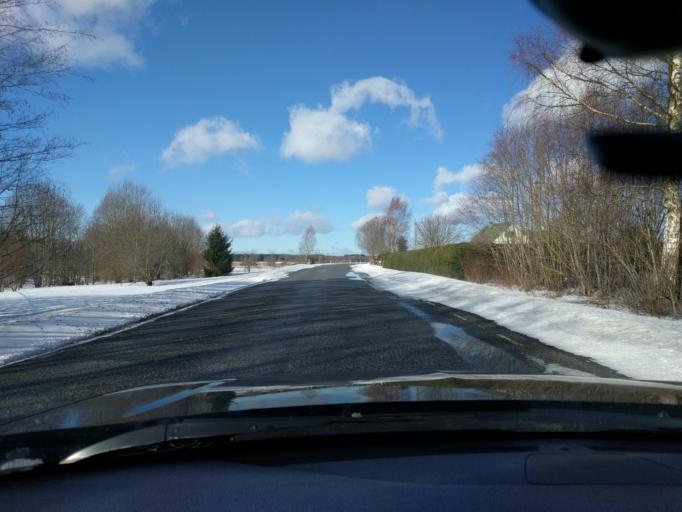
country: EE
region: Harju
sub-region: Raasiku vald
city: Raasiku
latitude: 59.3882
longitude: 25.1921
